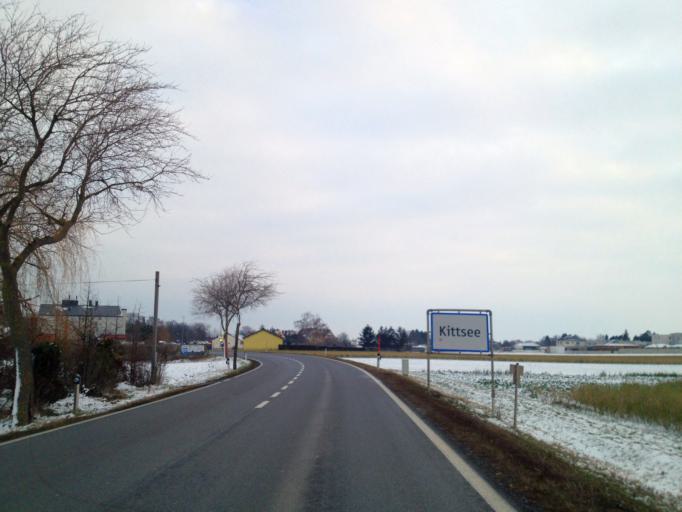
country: AT
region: Burgenland
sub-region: Politischer Bezirk Neusiedl am See
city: Kittsee
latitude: 48.0953
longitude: 17.0530
